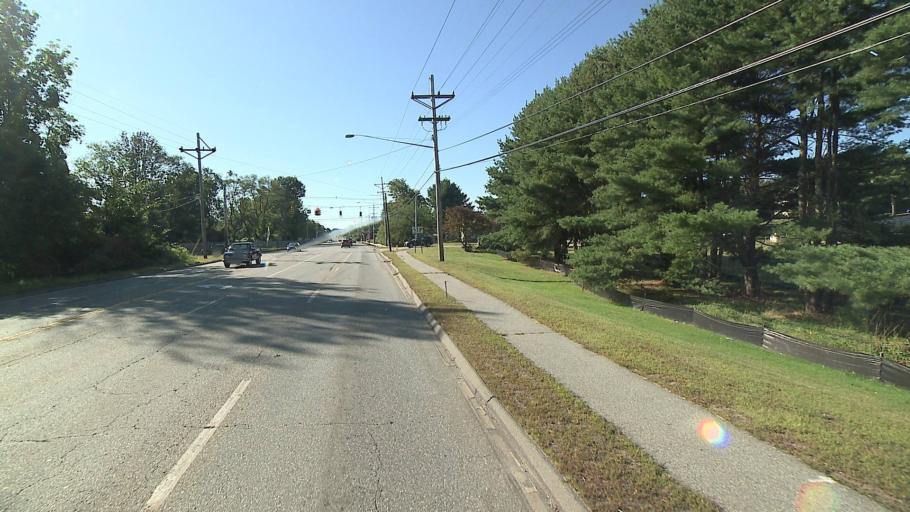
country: US
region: Connecticut
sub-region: New London County
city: Conning Towers-Nautilus Park
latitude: 41.3819
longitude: -72.0770
